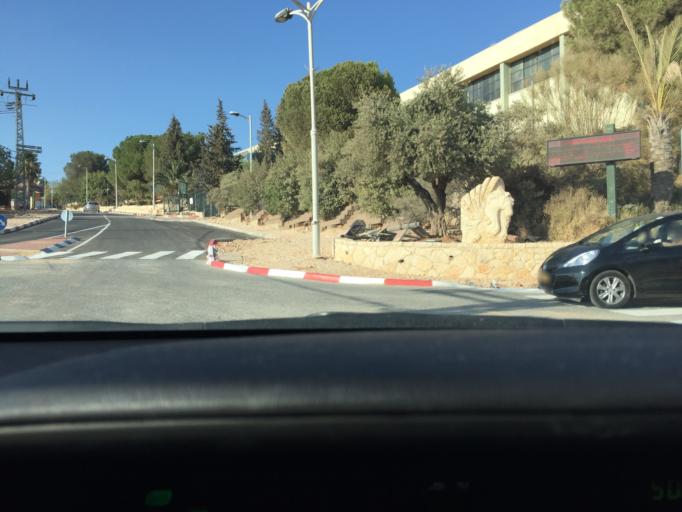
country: PS
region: West Bank
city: Al Lubban al Gharbi
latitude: 32.0338
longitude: 35.0504
